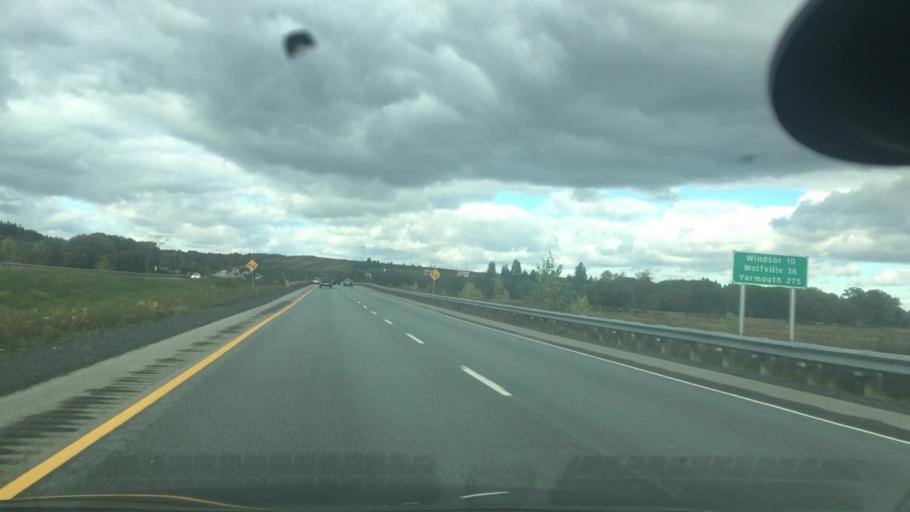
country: CA
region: Nova Scotia
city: Windsor
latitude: 44.9667
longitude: -64.0269
